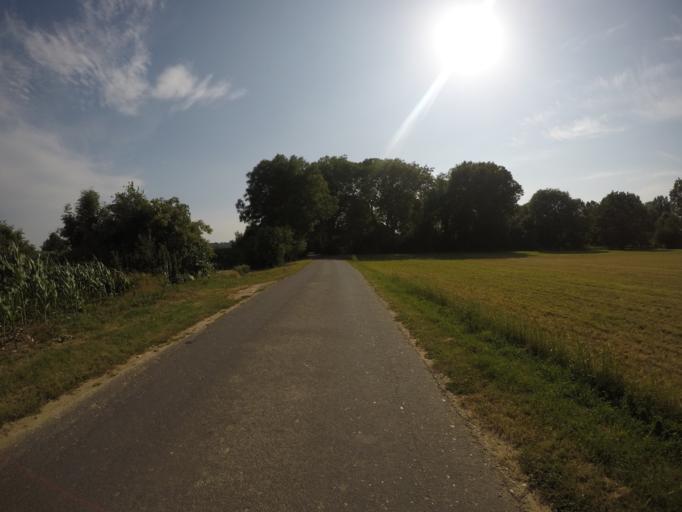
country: DE
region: North Rhine-Westphalia
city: Kalkar
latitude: 51.7357
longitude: 6.3194
